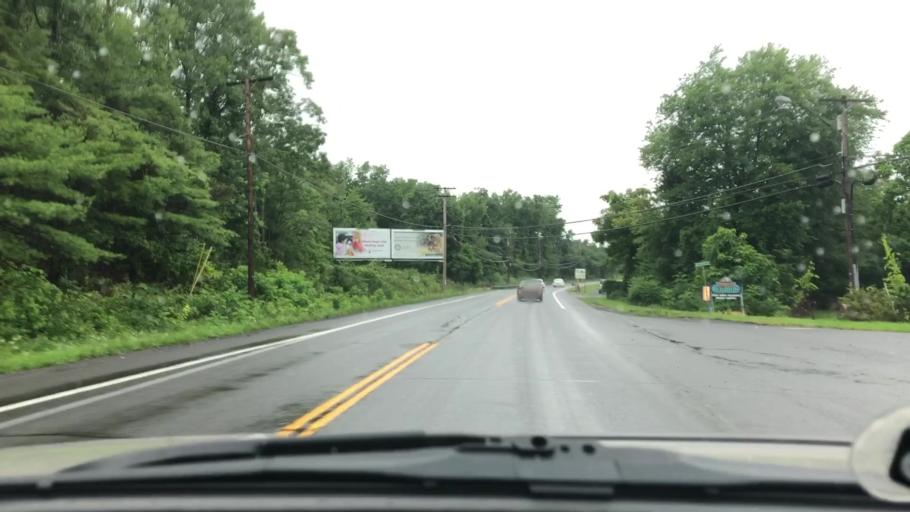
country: US
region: New York
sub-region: Ulster County
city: Manorville
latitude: 42.1234
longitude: -73.9945
